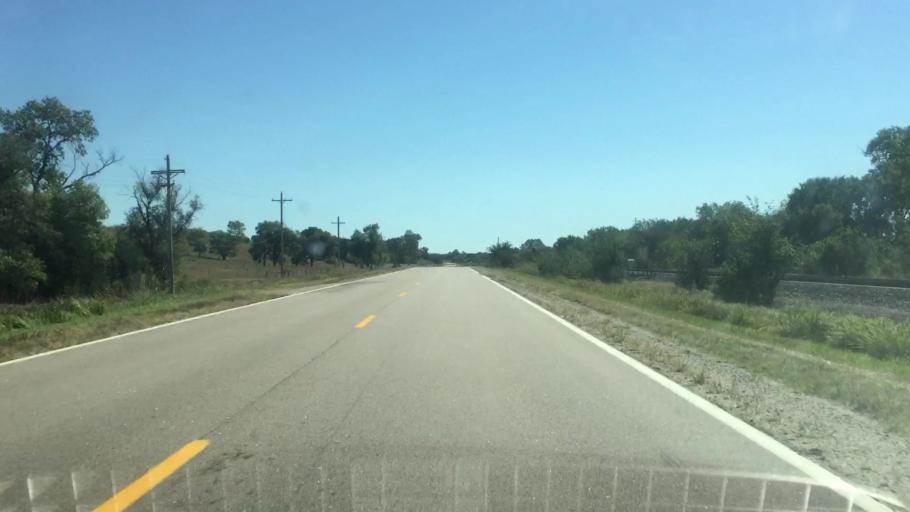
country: US
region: Nebraska
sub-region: Jefferson County
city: Fairbury
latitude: 40.0652
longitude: -97.0560
